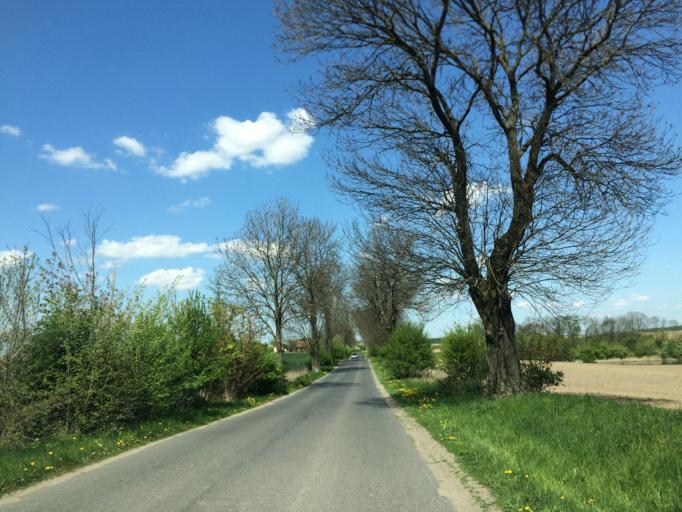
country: PL
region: Warmian-Masurian Voivodeship
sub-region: Powiat nowomiejski
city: Biskupiec
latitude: 53.4300
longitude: 19.2714
